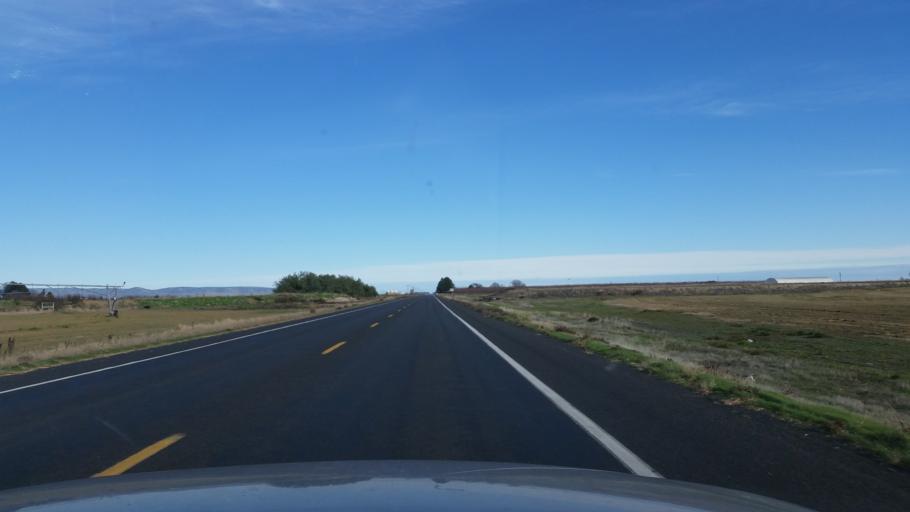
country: US
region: Washington
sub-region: Grant County
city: Quincy
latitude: 47.1236
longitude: -119.7995
